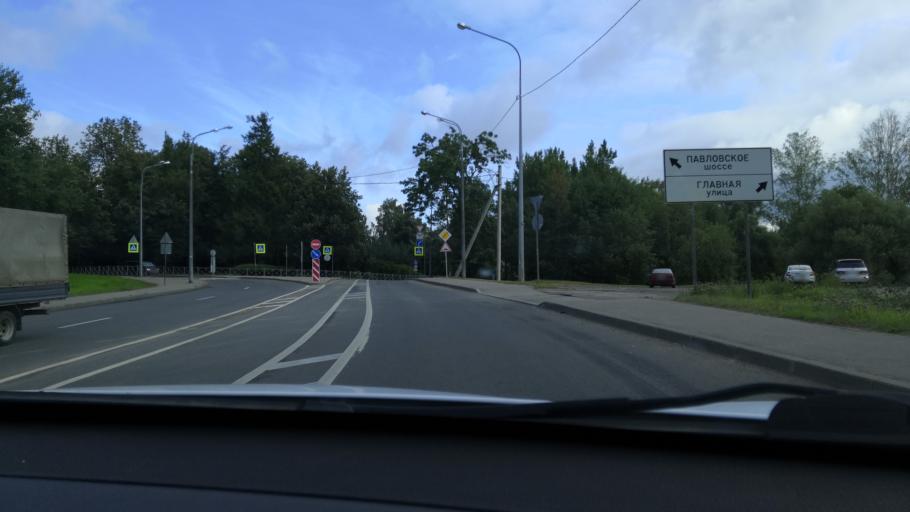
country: RU
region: St.-Petersburg
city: Pavlovsk
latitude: 59.6935
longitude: 30.4294
